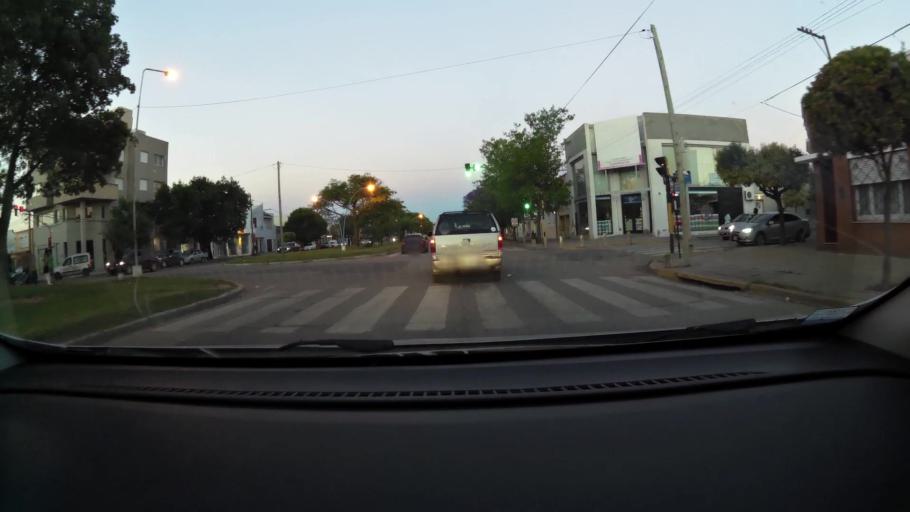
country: AR
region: Cordoba
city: Villa Maria
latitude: -32.4167
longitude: -63.2355
